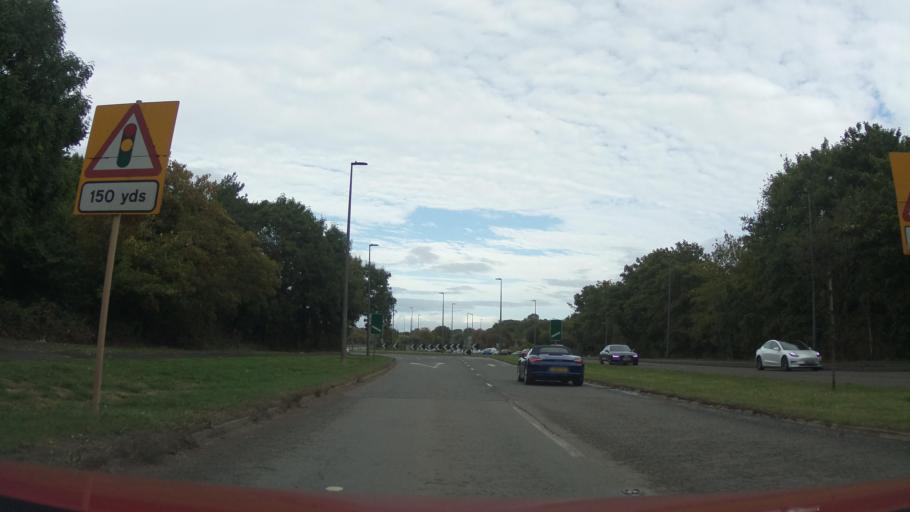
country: GB
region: England
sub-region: South Gloucestershire
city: Almondsbury
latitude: 51.5260
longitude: -2.6119
